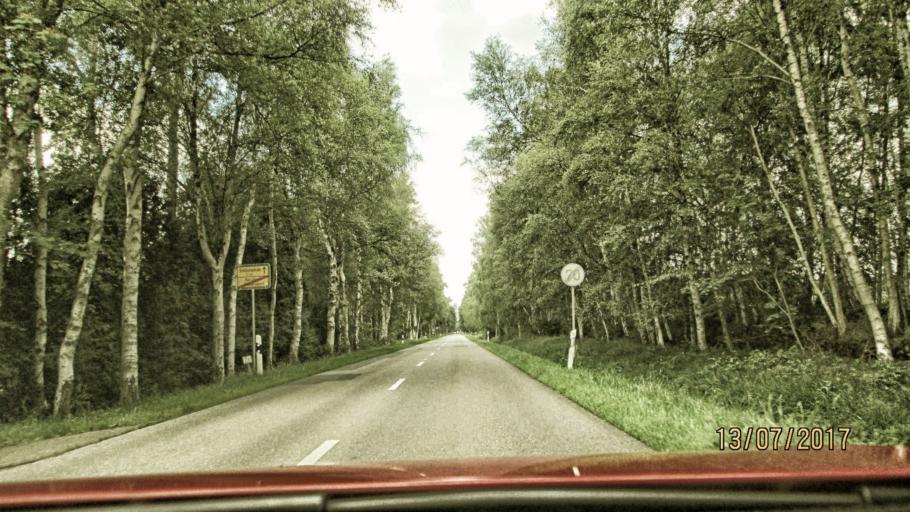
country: DE
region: Lower Saxony
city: Sassenburg
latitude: 52.5545
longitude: 10.6192
